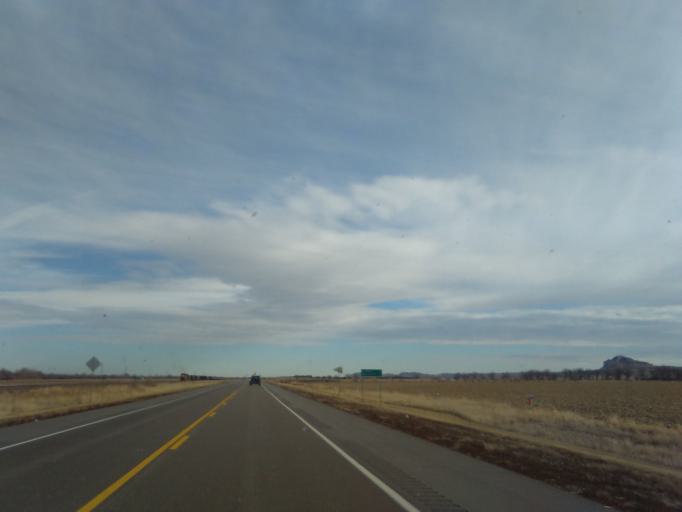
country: US
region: Nebraska
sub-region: Scotts Bluff County
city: Gering
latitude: 41.7819
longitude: -103.5123
